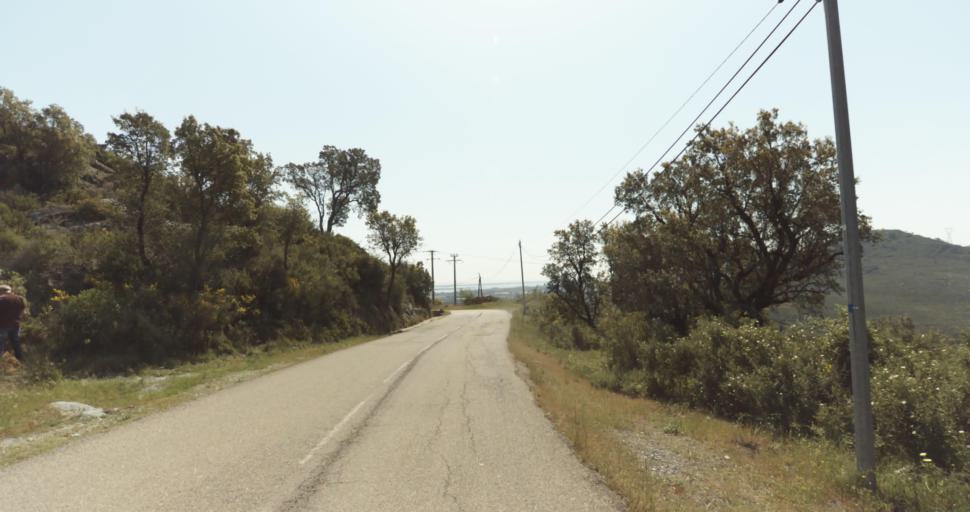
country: FR
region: Corsica
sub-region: Departement de la Haute-Corse
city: Biguglia
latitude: 42.6143
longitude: 9.4178
